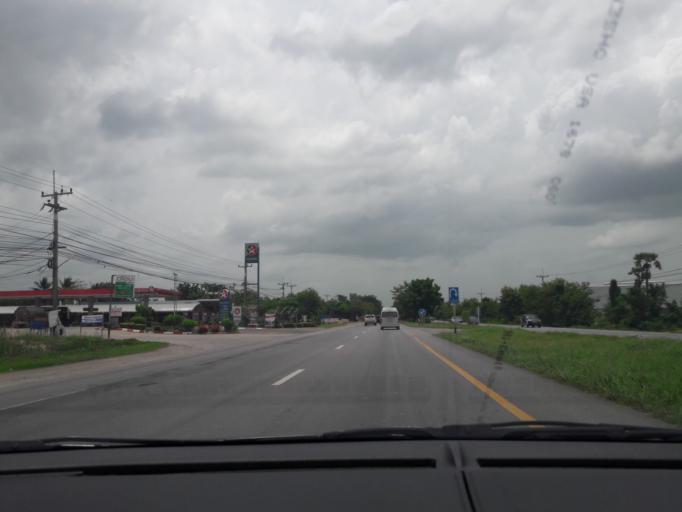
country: TH
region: Nakhon Ratchasima
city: Chaloem Phra Kiat
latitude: 15.0783
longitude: 102.2231
